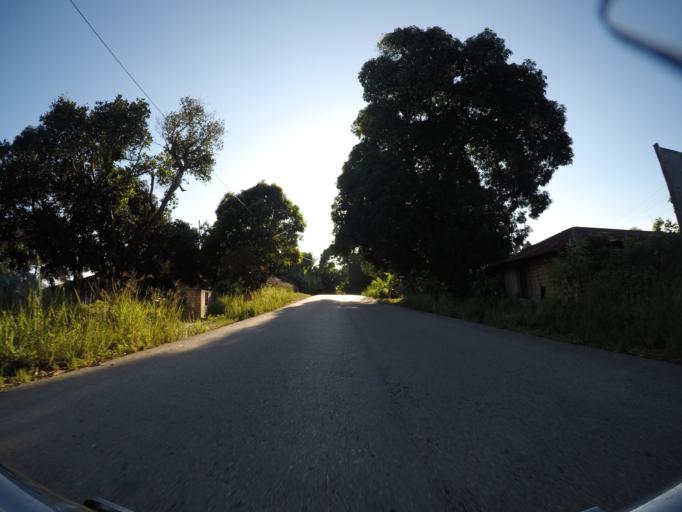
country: TZ
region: Pemba South
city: Mtambile
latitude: -5.3317
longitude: 39.7338
